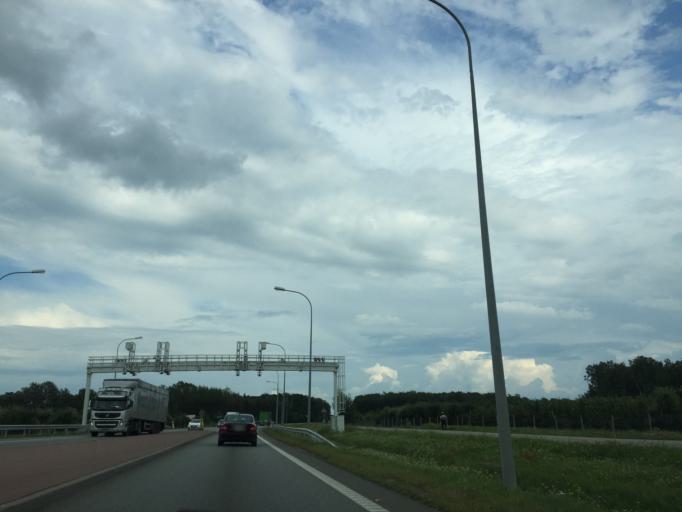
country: PL
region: Masovian Voivodeship
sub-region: Powiat grojecki
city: Grojec
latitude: 51.8761
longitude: 20.9082
